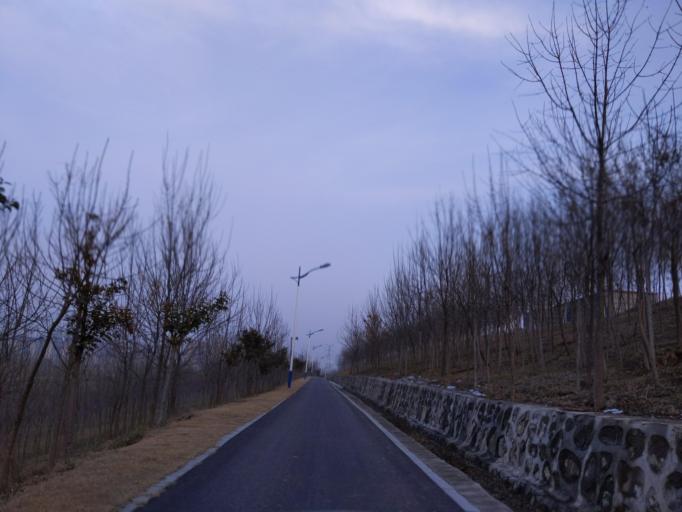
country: CN
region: Henan Sheng
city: Zhongyuanlu
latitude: 35.8189
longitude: 115.0460
